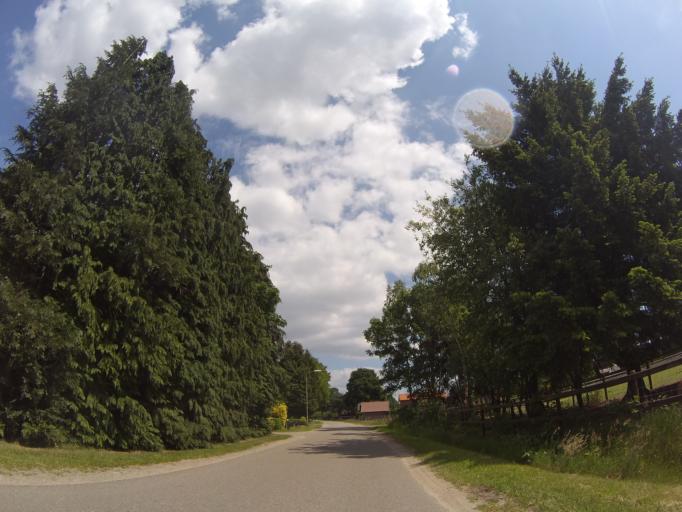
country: NL
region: Gelderland
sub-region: Gemeente Barneveld
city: Garderen
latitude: 52.2310
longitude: 5.6625
